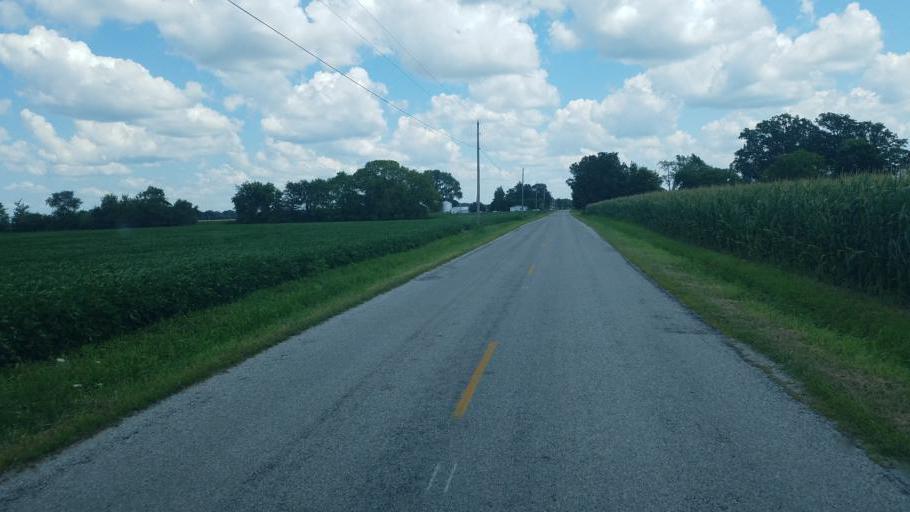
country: US
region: Ohio
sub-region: Marion County
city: Marion
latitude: 40.6380
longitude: -83.0023
